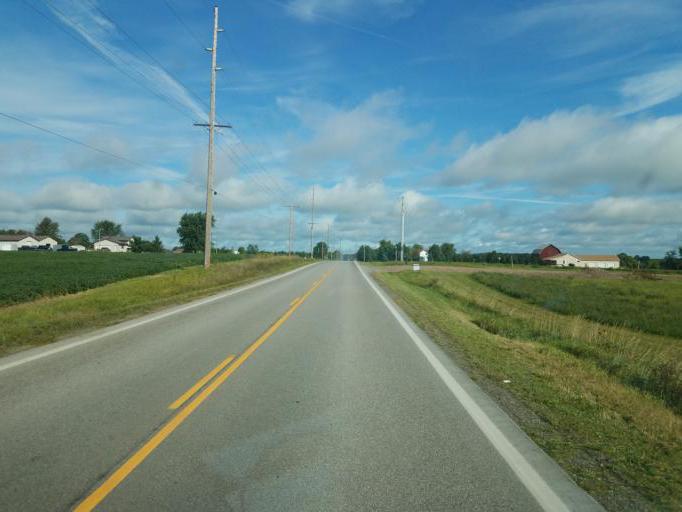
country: US
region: Ohio
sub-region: Wayne County
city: West Salem
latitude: 41.0118
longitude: -82.1184
